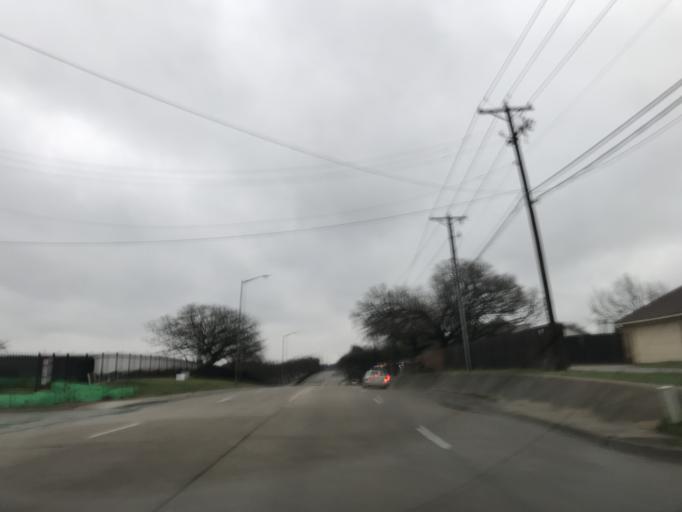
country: US
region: Texas
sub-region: Tarrant County
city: Arlington
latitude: 32.7754
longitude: -97.1032
